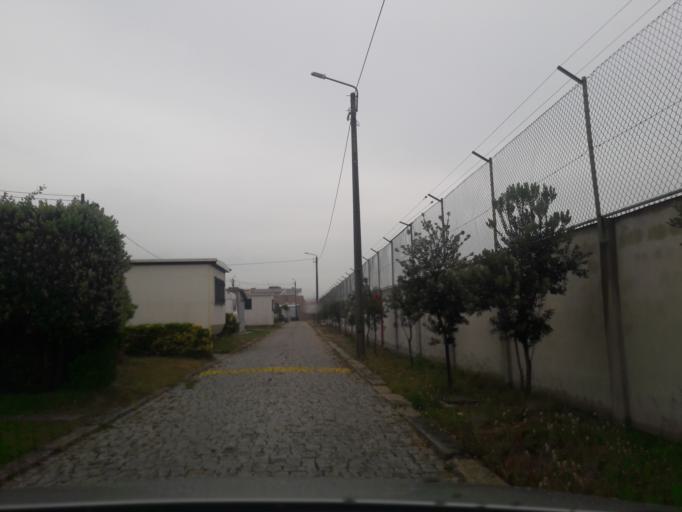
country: PT
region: Porto
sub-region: Vila do Conde
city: Vila do Conde
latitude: 41.3361
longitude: -8.7393
